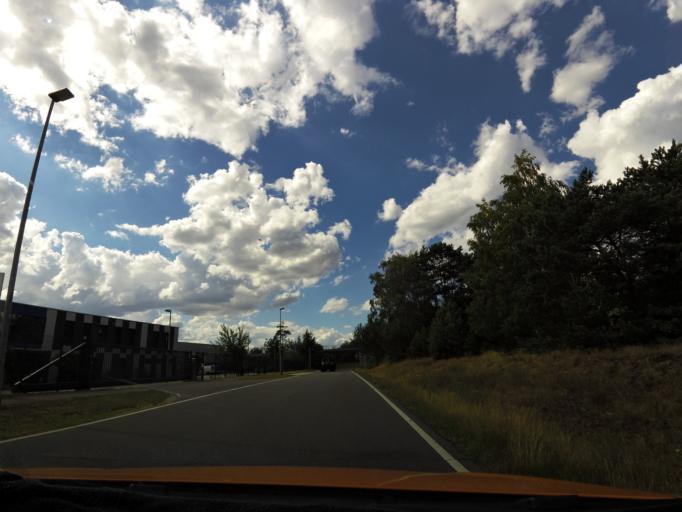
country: DE
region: Brandenburg
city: Konigs Wusterhausen
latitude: 52.3038
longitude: 13.6765
